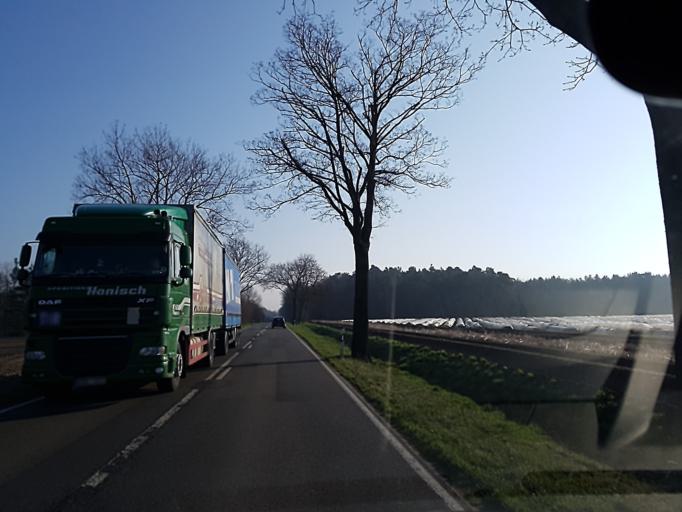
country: DE
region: Brandenburg
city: Calau
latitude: 51.7623
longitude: 14.0077
